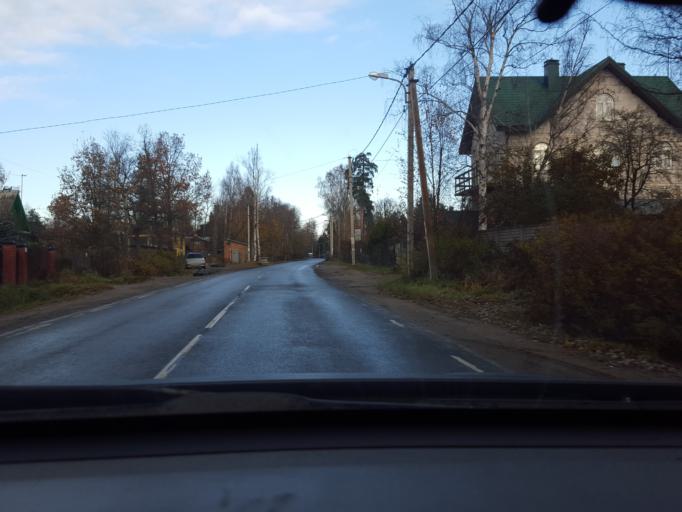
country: RU
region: St.-Petersburg
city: Shuvalovo
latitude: 60.0465
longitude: 30.2954
